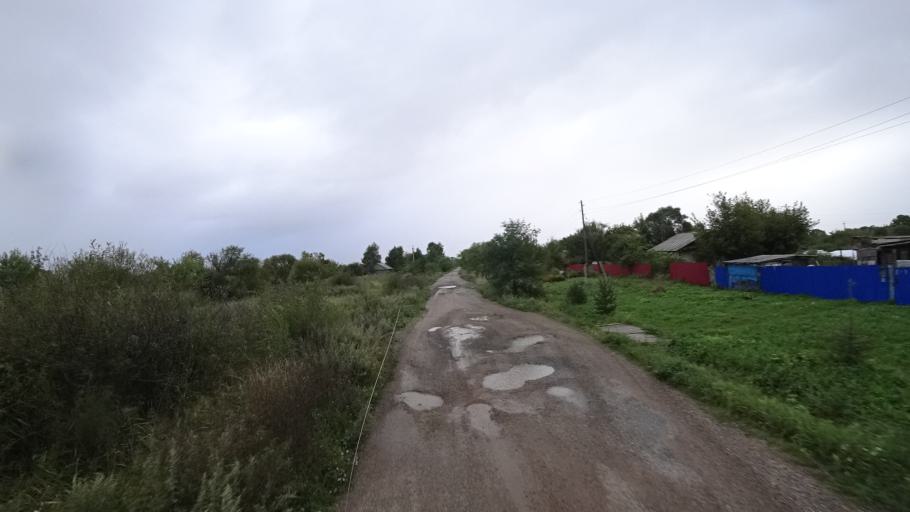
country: RU
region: Primorskiy
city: Chernigovka
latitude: 44.3982
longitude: 132.5293
